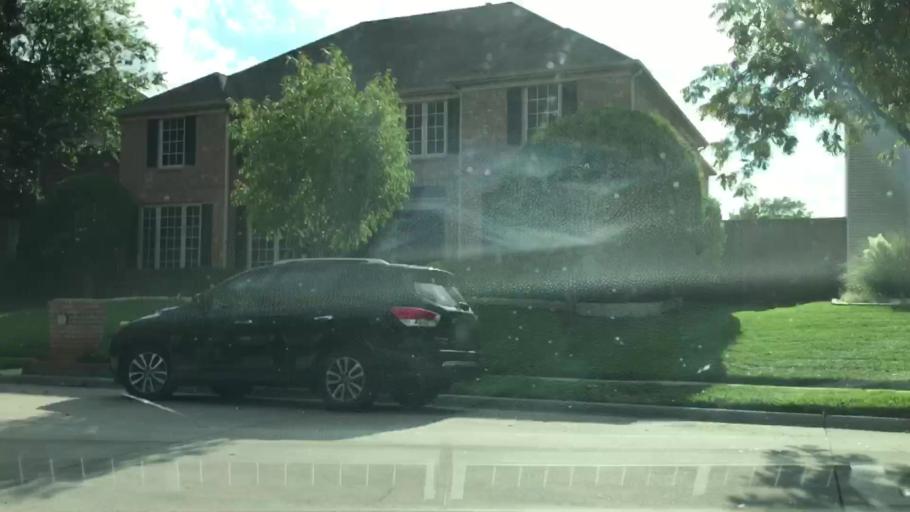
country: US
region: Texas
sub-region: Dallas County
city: Coppell
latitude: 32.9152
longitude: -96.9747
